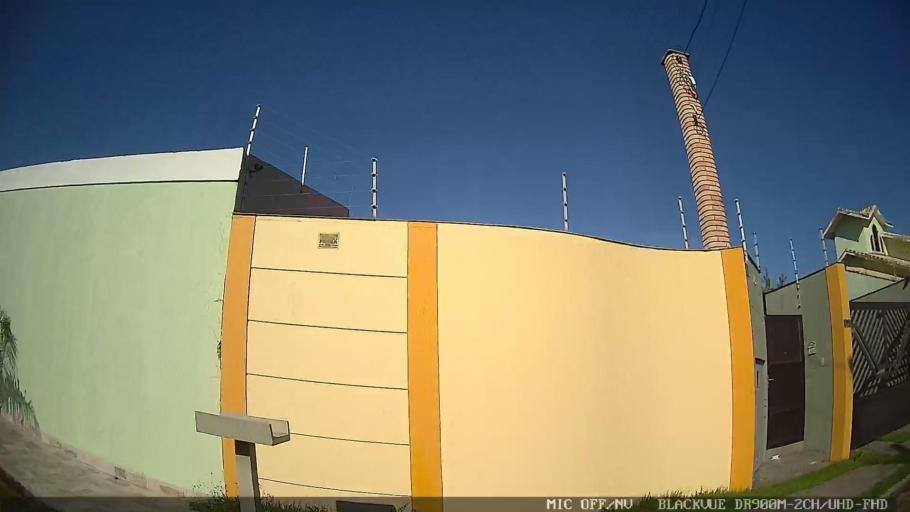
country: BR
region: Sao Paulo
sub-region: Peruibe
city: Peruibe
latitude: -24.2813
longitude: -46.9475
